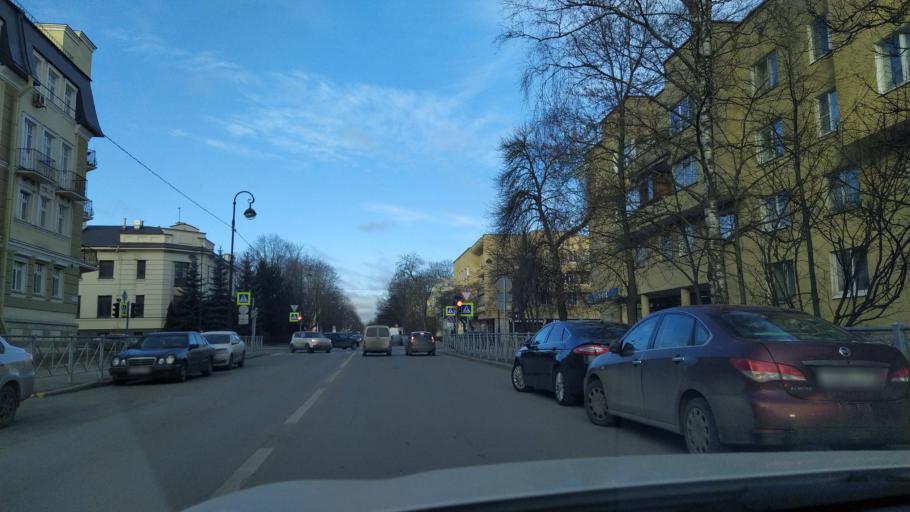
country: RU
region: St.-Petersburg
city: Pushkin
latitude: 59.7192
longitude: 30.4141
